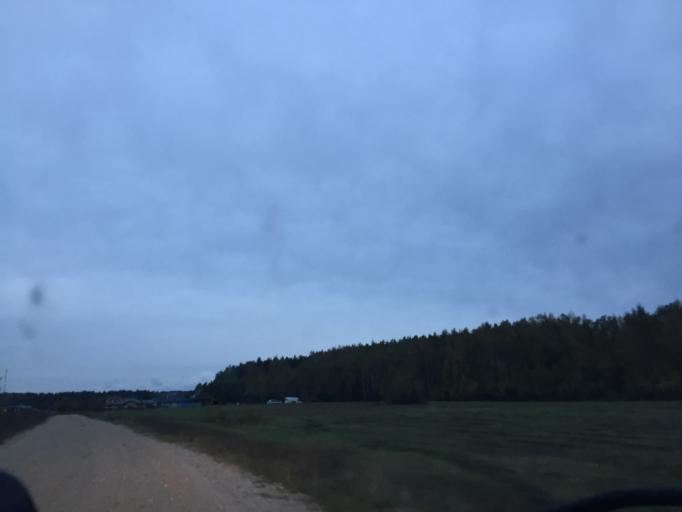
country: LV
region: Garkalne
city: Garkalne
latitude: 57.0832
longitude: 24.3804
